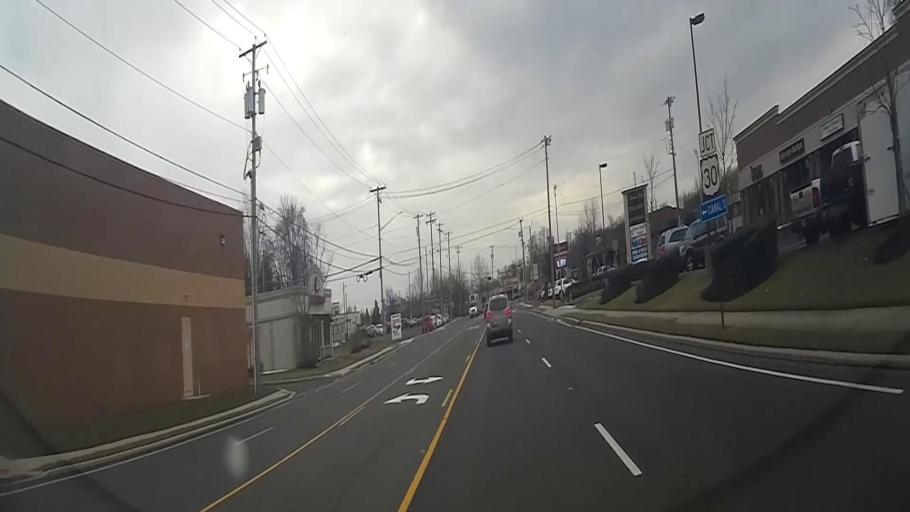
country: US
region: New Jersey
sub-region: Camden County
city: Berlin
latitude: 39.7998
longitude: -74.9324
